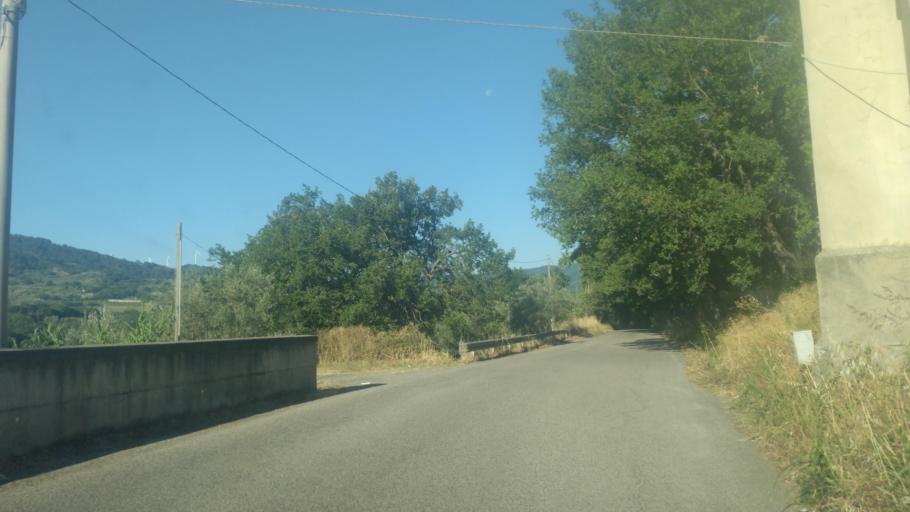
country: IT
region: Calabria
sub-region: Provincia di Catanzaro
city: Squillace
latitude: 38.7757
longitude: 16.5100
